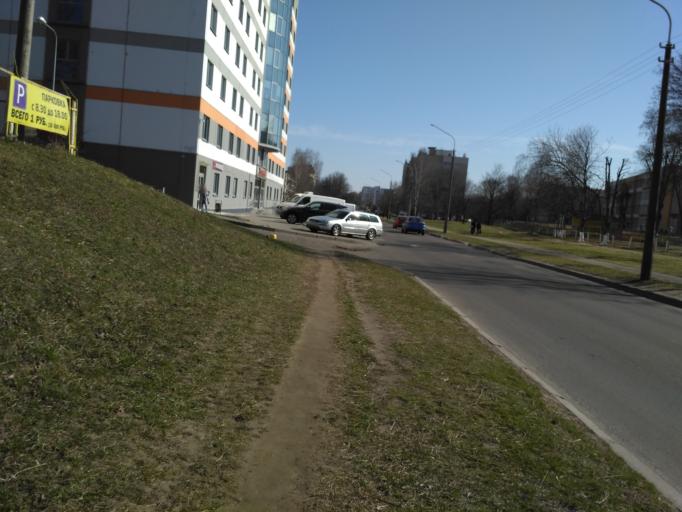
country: BY
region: Minsk
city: Novoye Medvezhino
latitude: 53.9060
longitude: 27.5021
